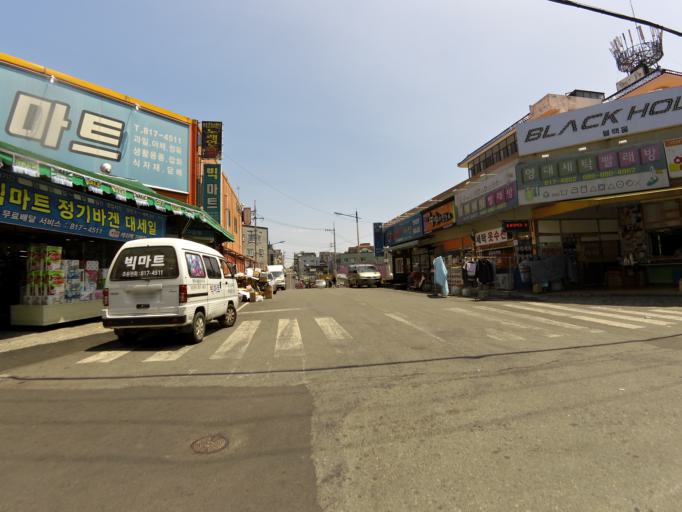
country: KR
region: Gyeongsangbuk-do
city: Gyeongsan-si
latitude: 35.8394
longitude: 128.7541
